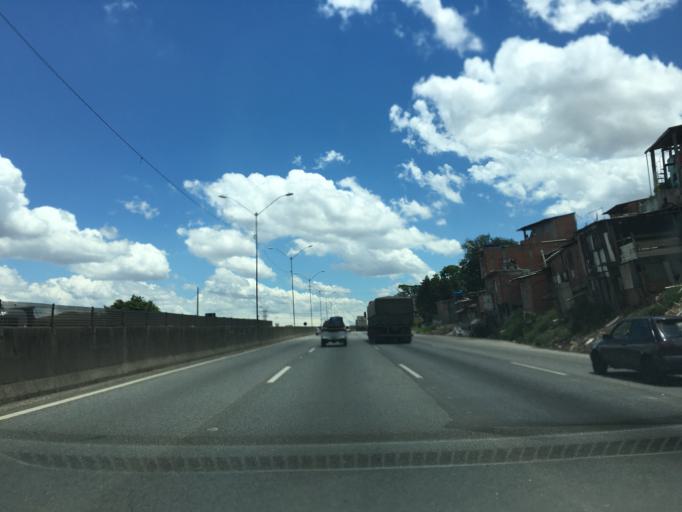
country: BR
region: Sao Paulo
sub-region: Guarulhos
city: Guarulhos
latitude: -23.4505
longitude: -46.5700
